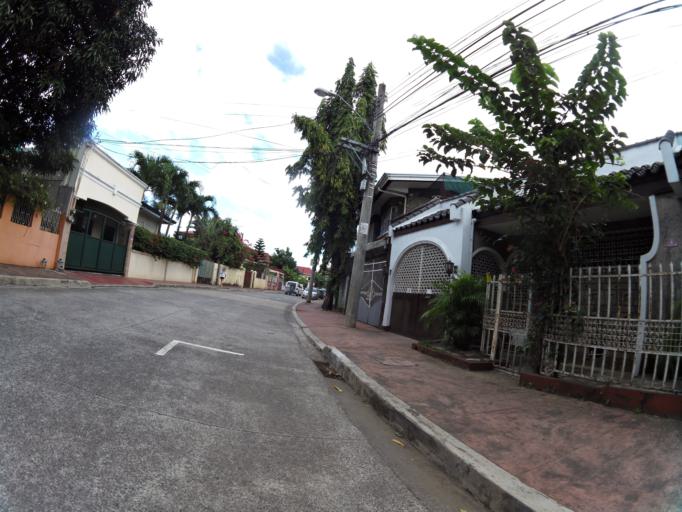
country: PH
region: Calabarzon
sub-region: Province of Rizal
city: Antipolo
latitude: 14.6389
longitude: 121.1135
